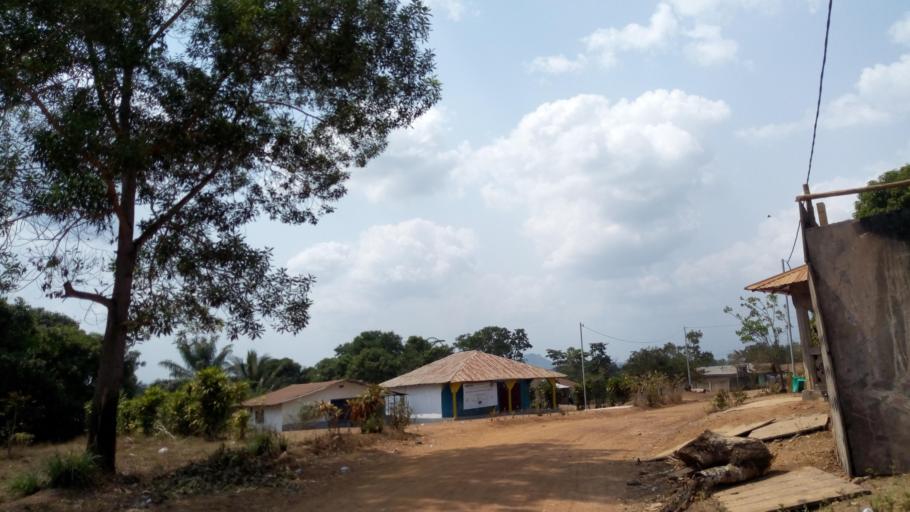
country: SL
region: Southern Province
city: Mogbwemo
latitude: 7.7938
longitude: -12.2999
